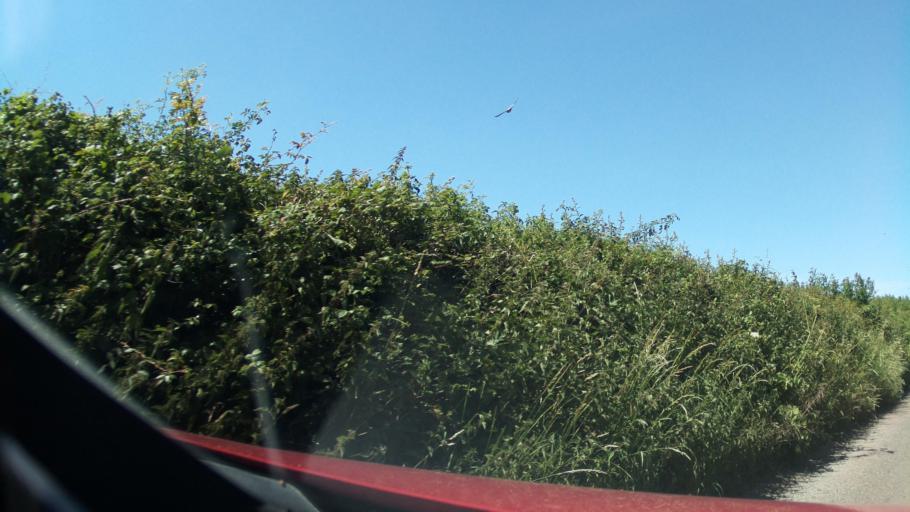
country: GB
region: England
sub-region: Borough of Torbay
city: Paignton
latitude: 50.4059
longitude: -3.5862
